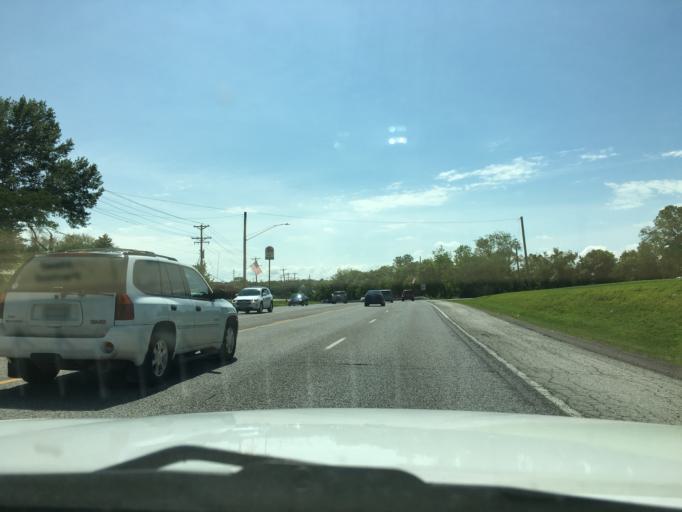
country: US
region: Missouri
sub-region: Franklin County
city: Union
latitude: 38.4444
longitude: -90.9998
